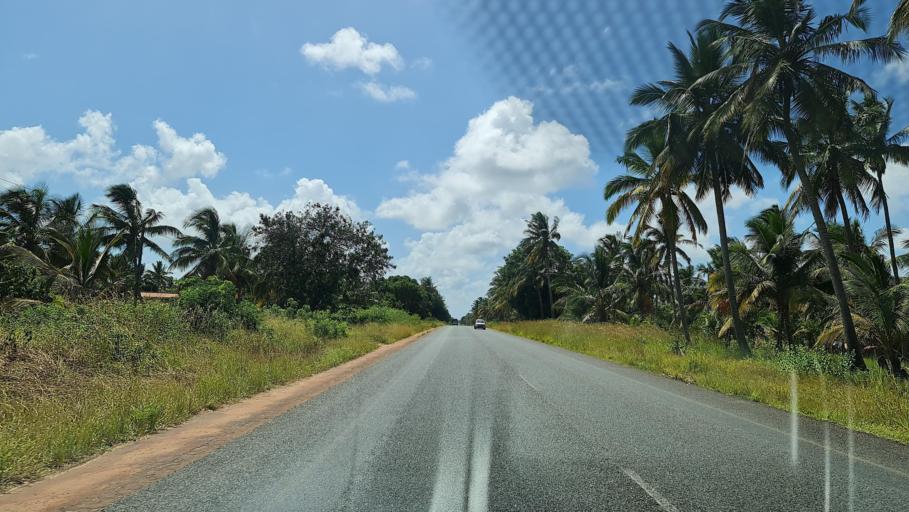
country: MZ
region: Inhambane
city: Maxixe
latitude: -24.5424
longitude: 34.8983
